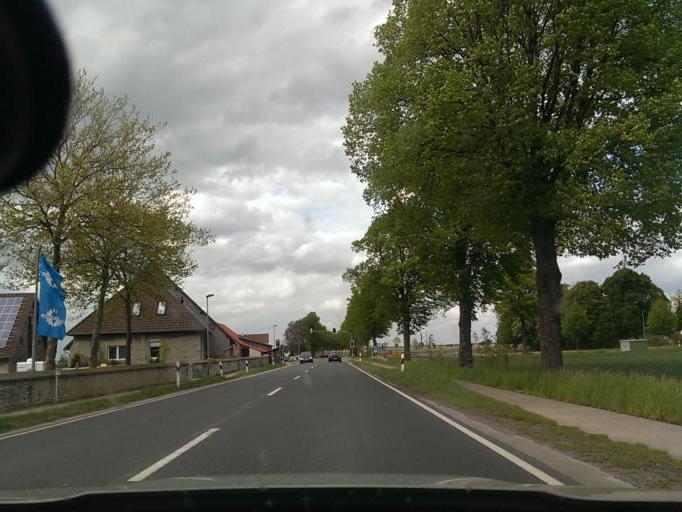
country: DE
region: Lower Saxony
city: Pattensen
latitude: 52.2152
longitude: 9.7469
